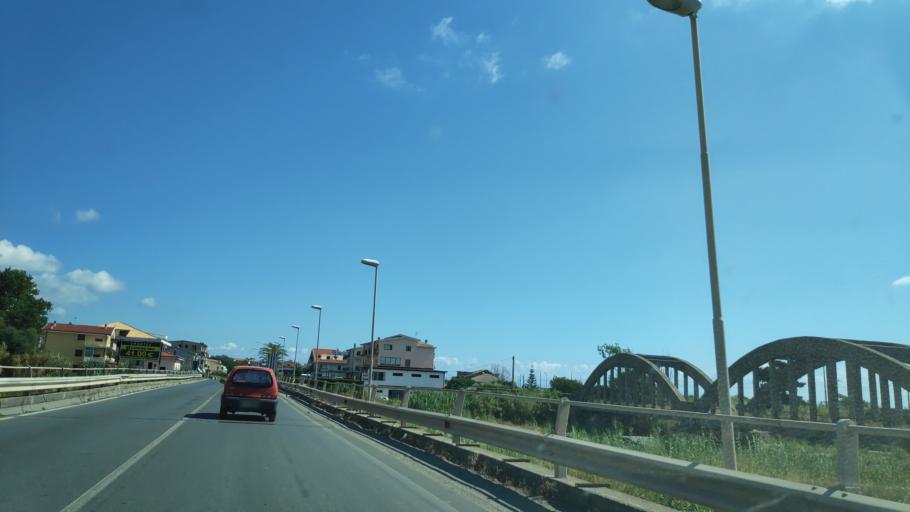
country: IT
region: Calabria
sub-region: Provincia di Cosenza
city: Campora San Giovanni
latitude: 39.0781
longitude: 16.0891
